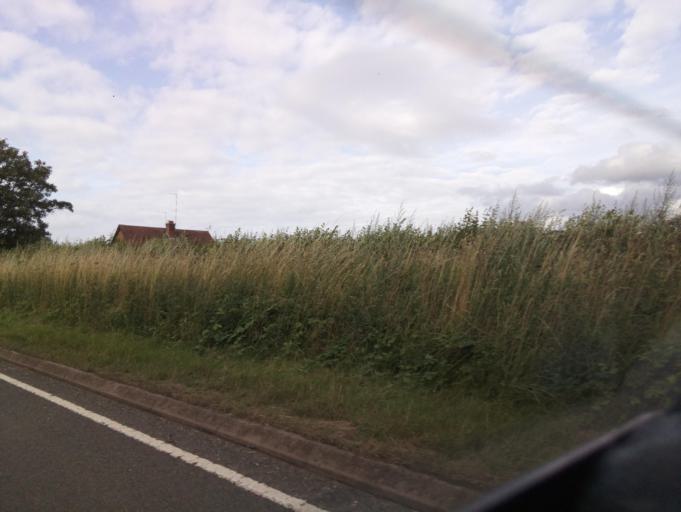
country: GB
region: England
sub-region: Warwickshire
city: Dunchurch
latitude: 52.3293
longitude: -1.2988
